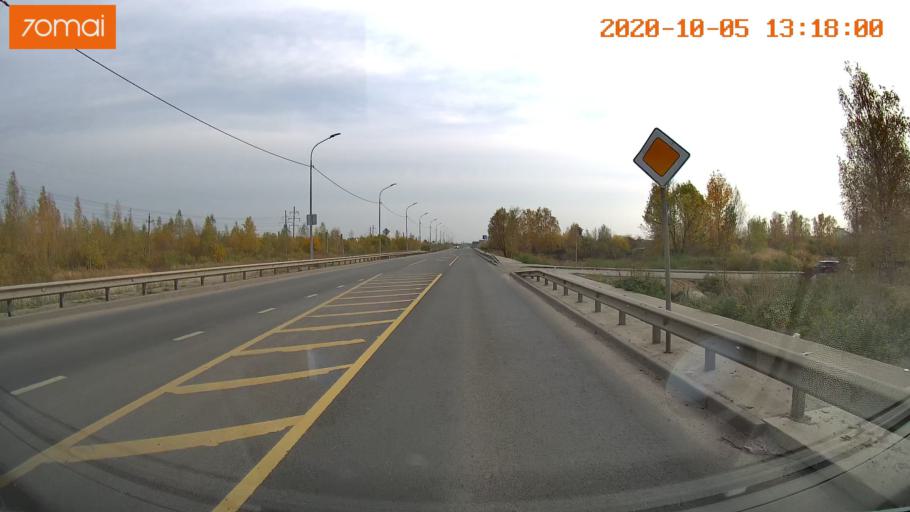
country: RU
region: Ivanovo
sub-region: Gorod Ivanovo
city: Ivanovo
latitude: 56.9812
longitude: 40.9155
